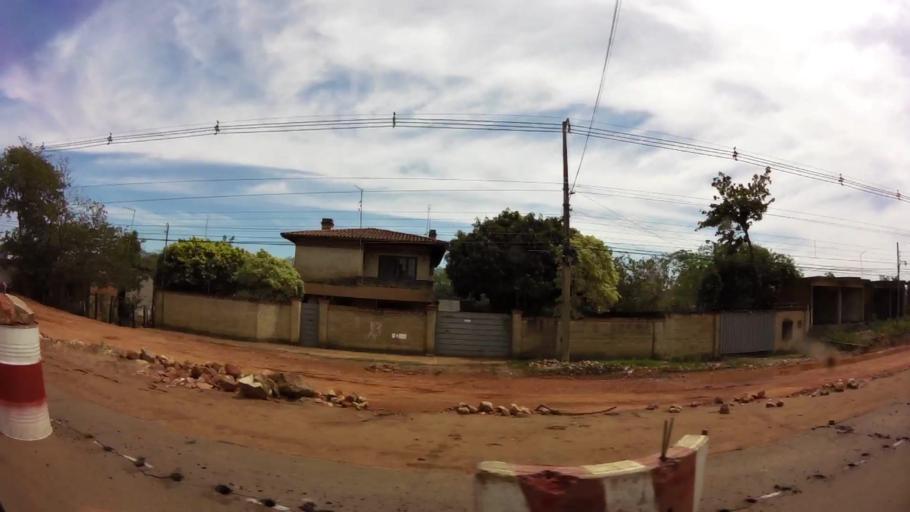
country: PY
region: Central
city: Limpio
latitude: -25.1962
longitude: -57.5129
